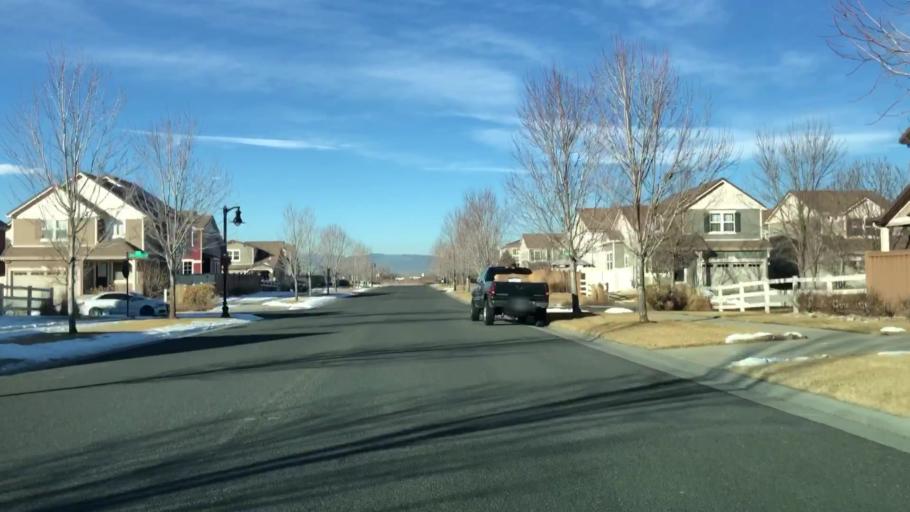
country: US
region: Colorado
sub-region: Larimer County
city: Loveland
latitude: 40.3907
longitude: -104.9880
